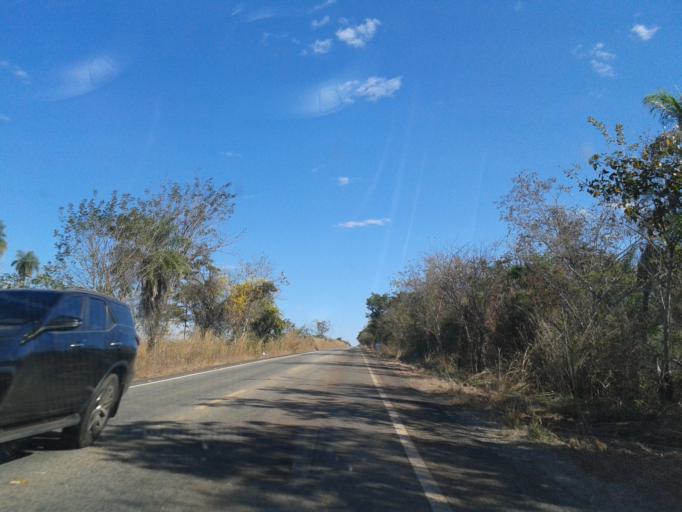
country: BR
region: Goias
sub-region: Mozarlandia
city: Mozarlandia
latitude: -14.5441
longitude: -50.4910
